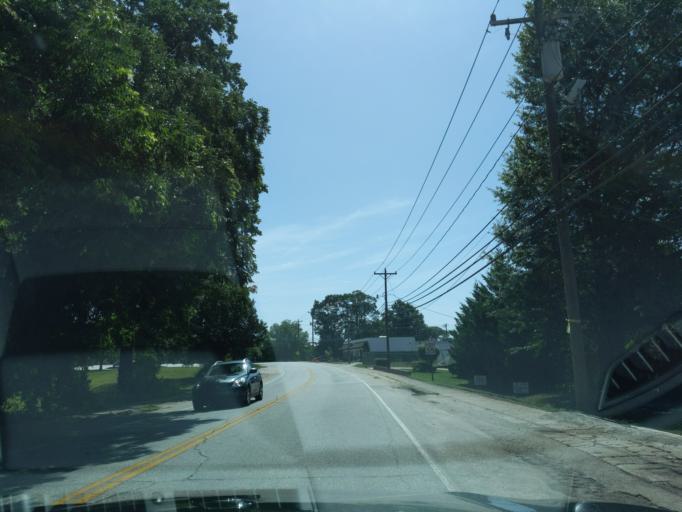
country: US
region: South Carolina
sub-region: Greenville County
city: Taylors
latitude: 34.9194
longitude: -82.3055
